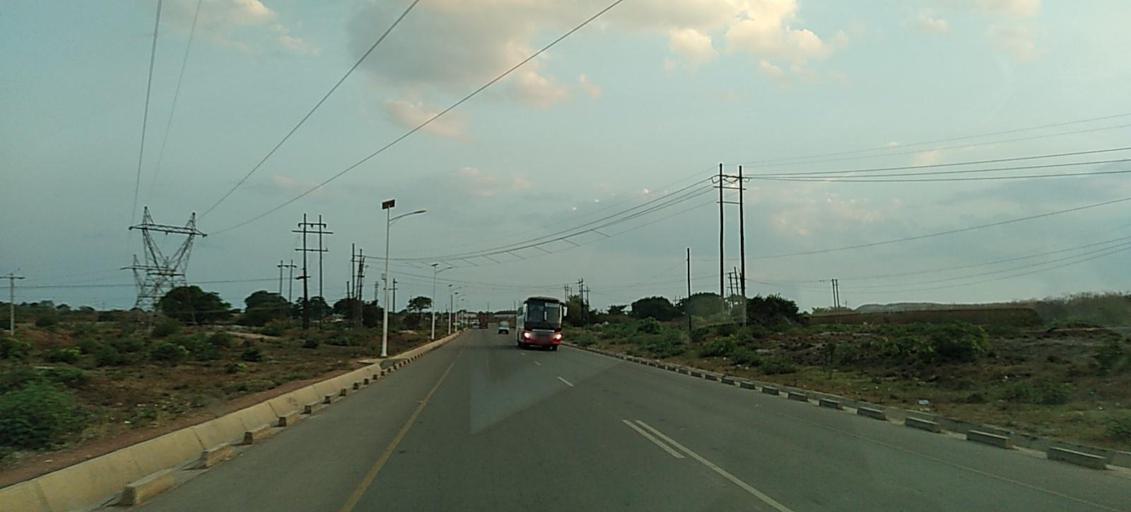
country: ZM
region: Copperbelt
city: Chingola
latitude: -12.5343
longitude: 27.8385
